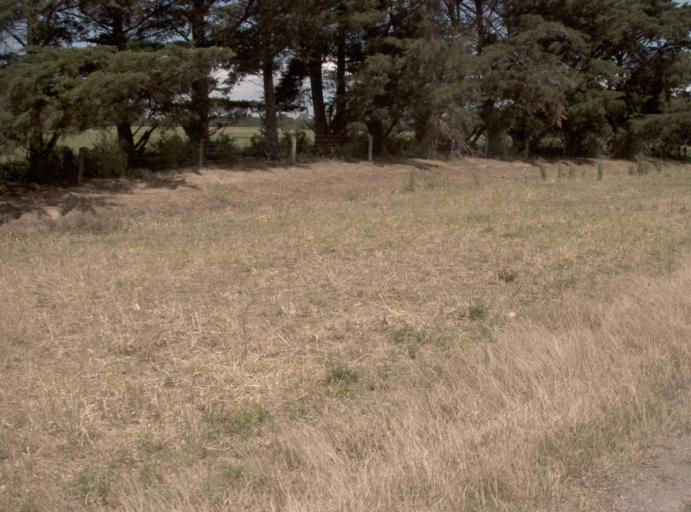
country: AU
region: Victoria
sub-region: Wellington
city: Heyfield
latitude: -37.9993
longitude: 146.8845
